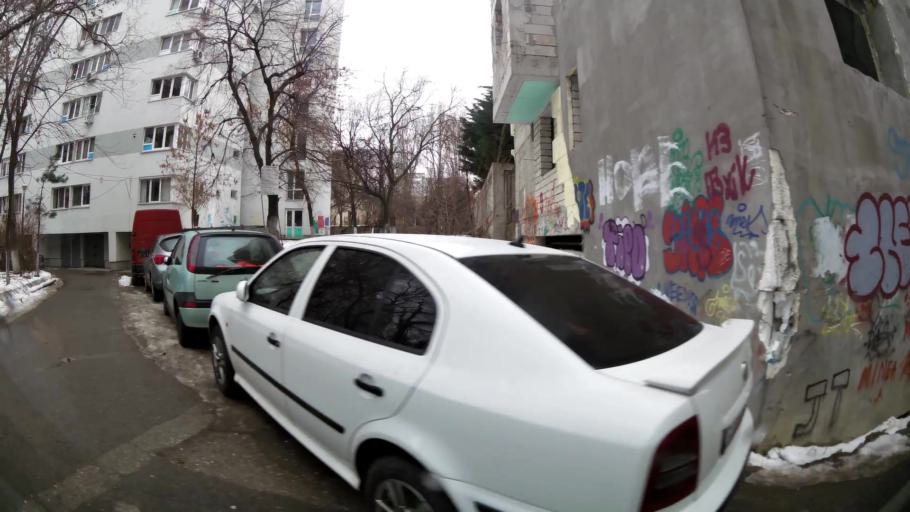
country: RO
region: Ilfov
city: Dobroesti
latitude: 44.4194
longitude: 26.1698
